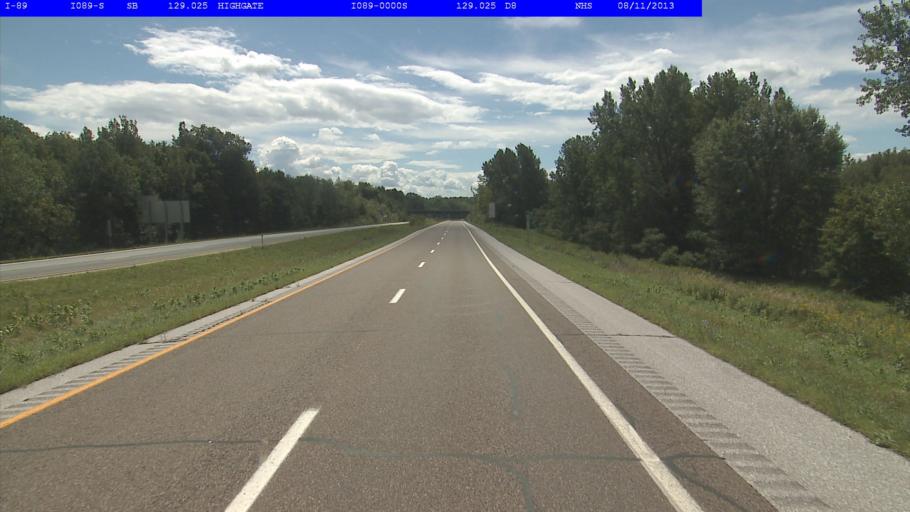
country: US
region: Vermont
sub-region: Franklin County
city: Swanton
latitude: 44.9979
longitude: -73.0865
